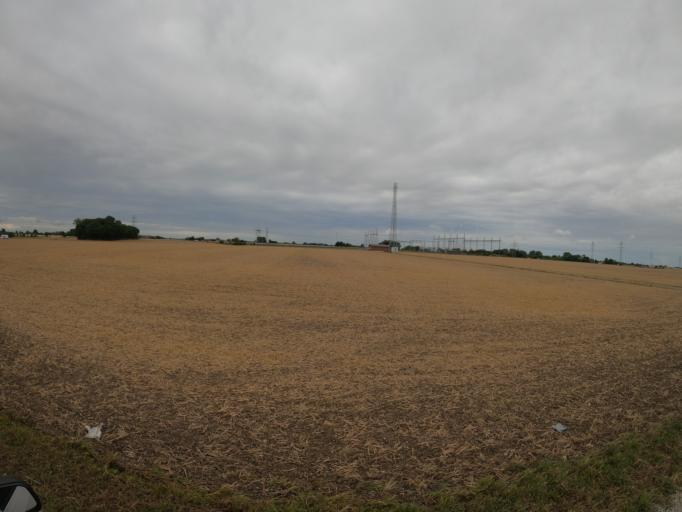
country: SE
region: Skane
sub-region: Lunds Kommun
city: Lund
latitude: 55.7406
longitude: 13.1496
